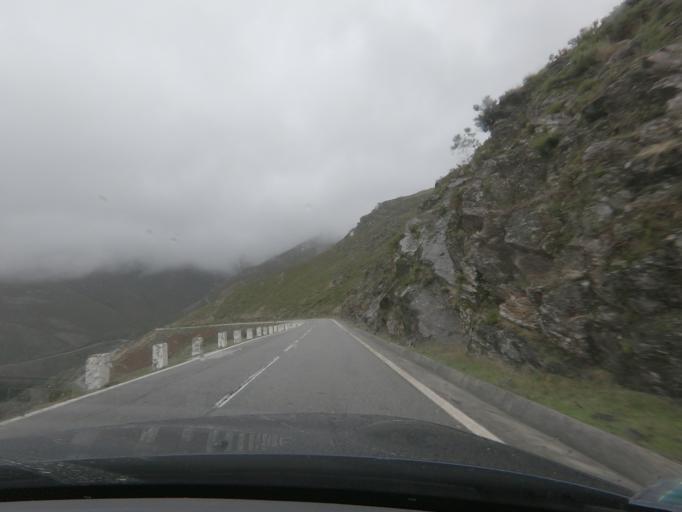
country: PT
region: Vila Real
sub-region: Mondim de Basto
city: Mondim de Basto
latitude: 41.3380
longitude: -7.8743
